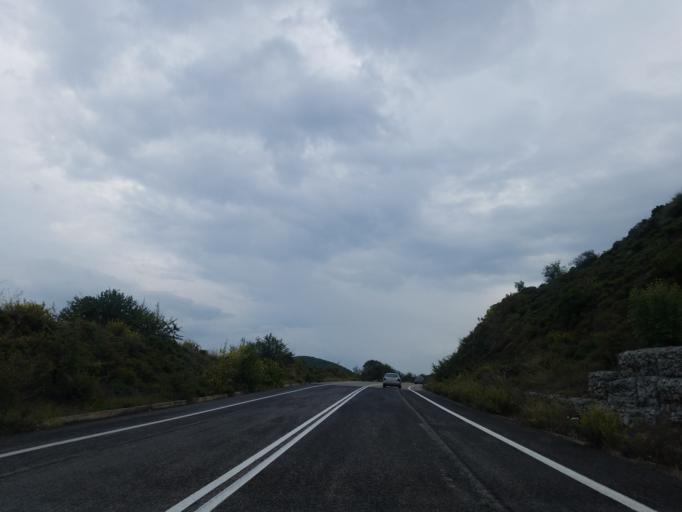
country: GR
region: Central Greece
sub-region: Nomos Voiotias
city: Livadeia
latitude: 38.4467
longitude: 22.7971
